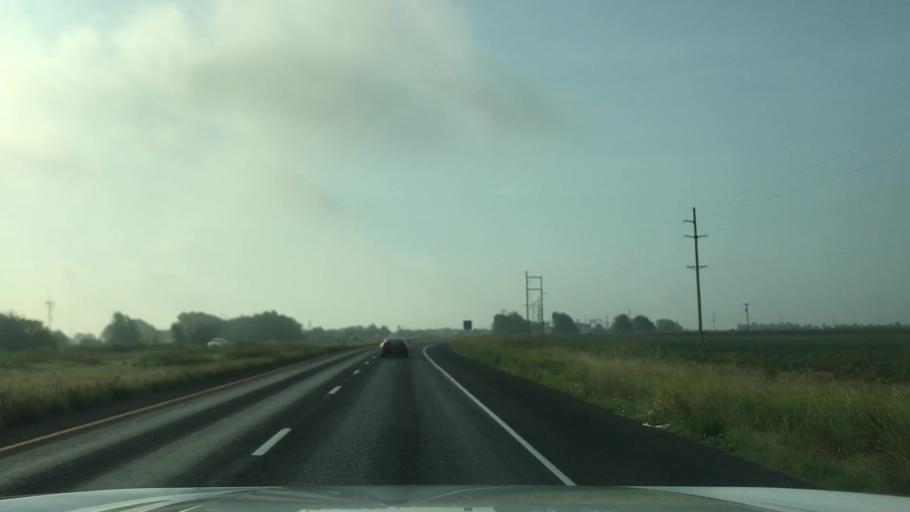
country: US
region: Texas
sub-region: Lubbock County
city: Slaton
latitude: 33.3620
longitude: -101.5597
